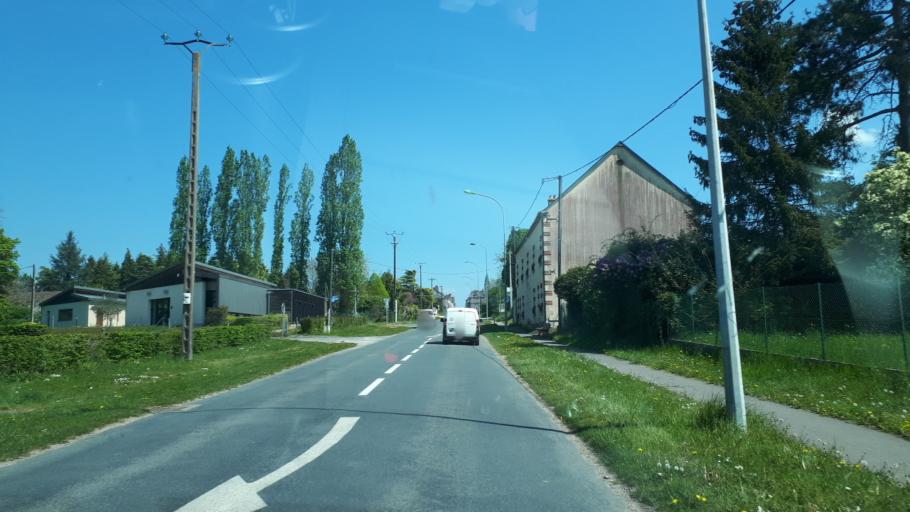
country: FR
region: Centre
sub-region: Departement du Cher
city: Henrichemont
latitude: 47.3001
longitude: 2.5177
